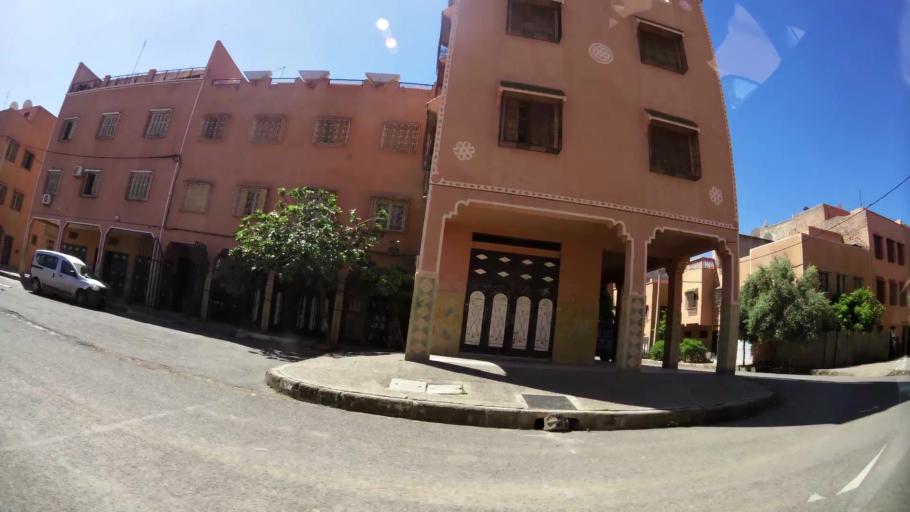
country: MA
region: Marrakech-Tensift-Al Haouz
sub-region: Marrakech
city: Marrakesh
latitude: 31.6370
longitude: -8.0694
